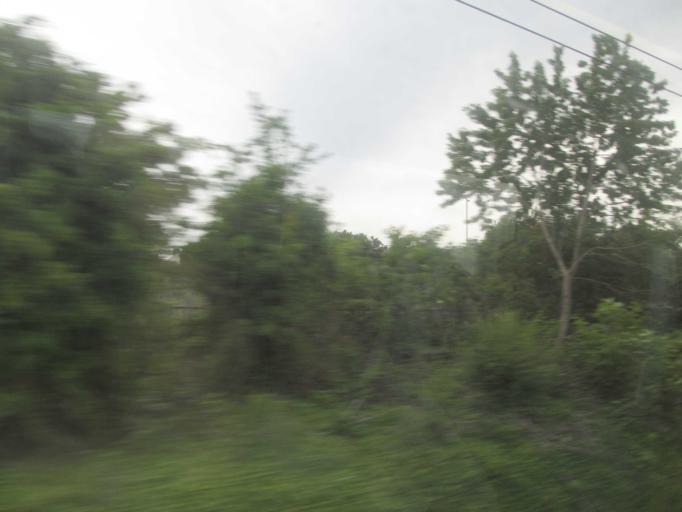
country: GB
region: England
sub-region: Bedford
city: Bedford
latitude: 52.1247
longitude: -0.4779
